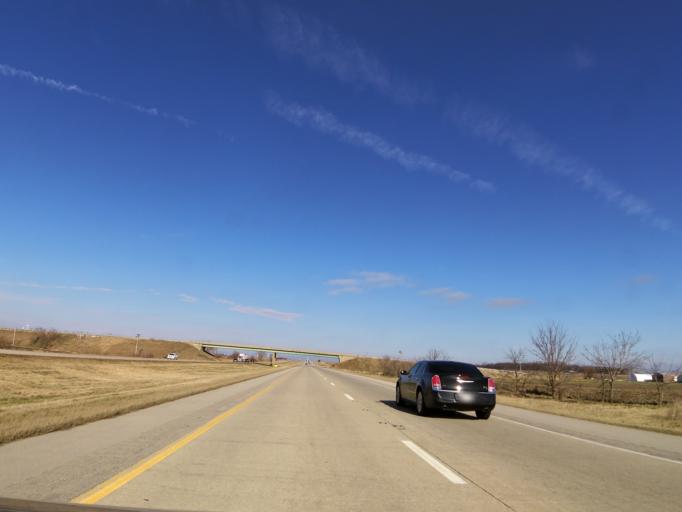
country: US
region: Illinois
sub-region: LaSalle County
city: Mendota
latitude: 41.5956
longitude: -89.0609
